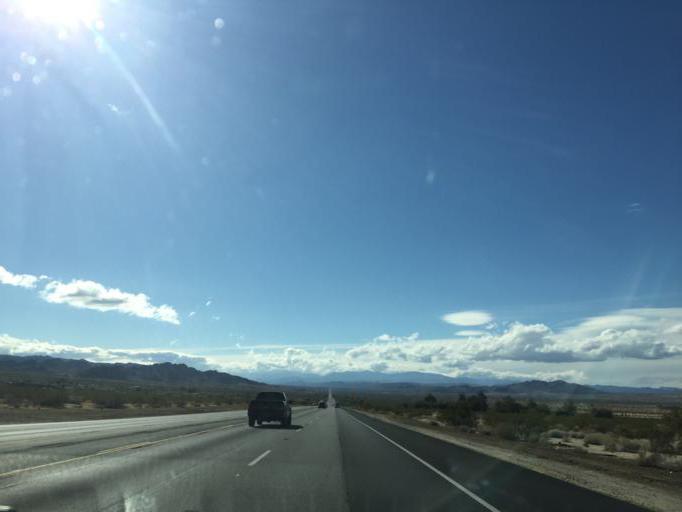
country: US
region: California
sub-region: San Bernardino County
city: Joshua Tree
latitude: 34.1352
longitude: -116.2071
